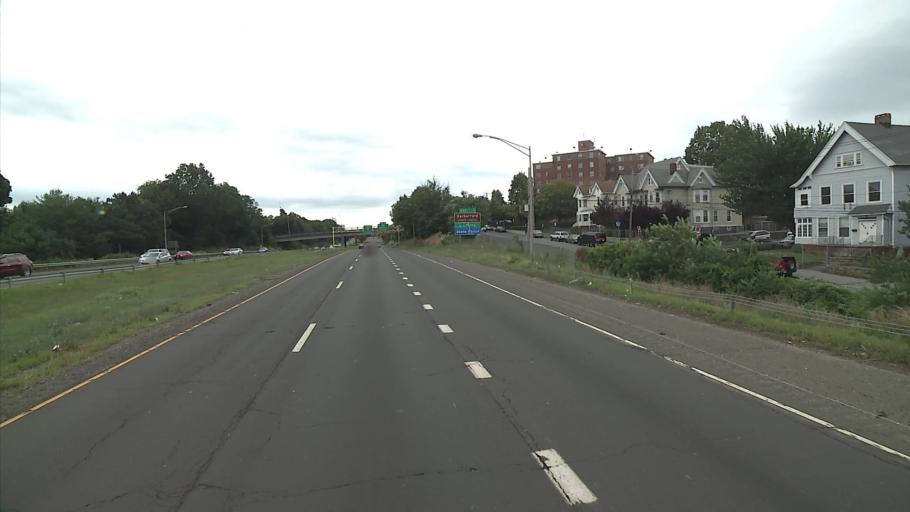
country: US
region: Connecticut
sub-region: Fairfield County
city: Bridgeport
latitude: 41.1849
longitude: -73.1934
